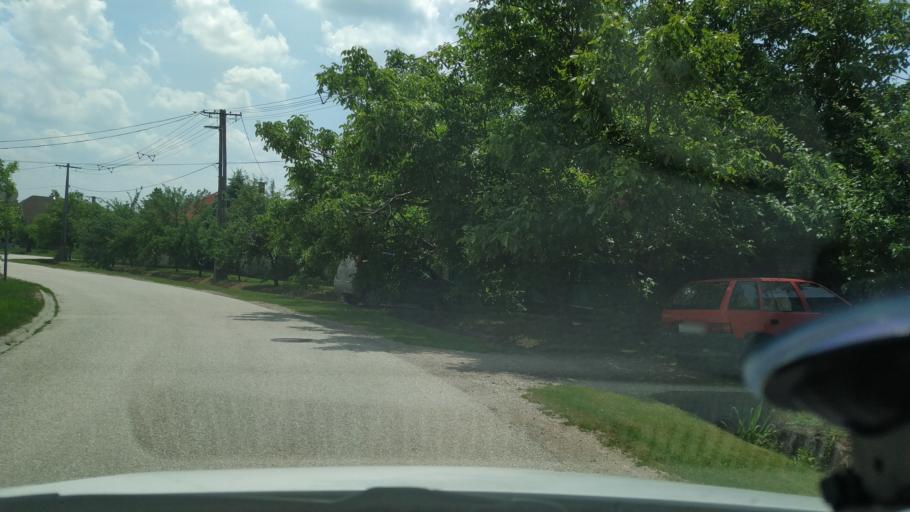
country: HU
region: Veszprem
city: Varpalota
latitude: 47.2006
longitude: 18.1807
